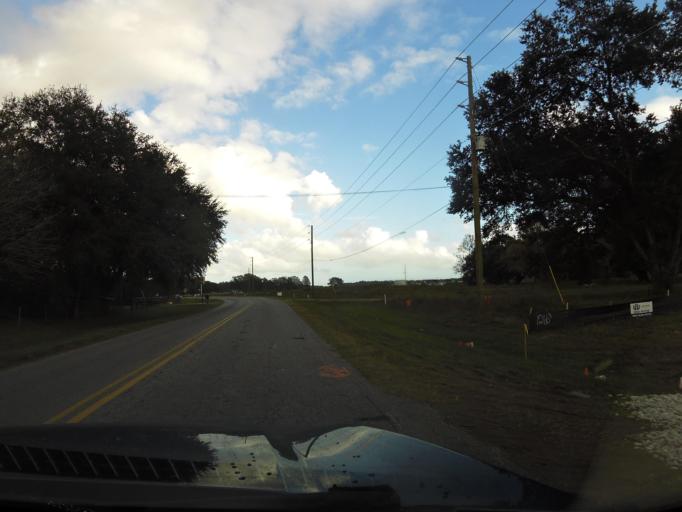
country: US
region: Florida
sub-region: Clay County
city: Asbury Lake
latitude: 30.0464
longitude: -81.7776
